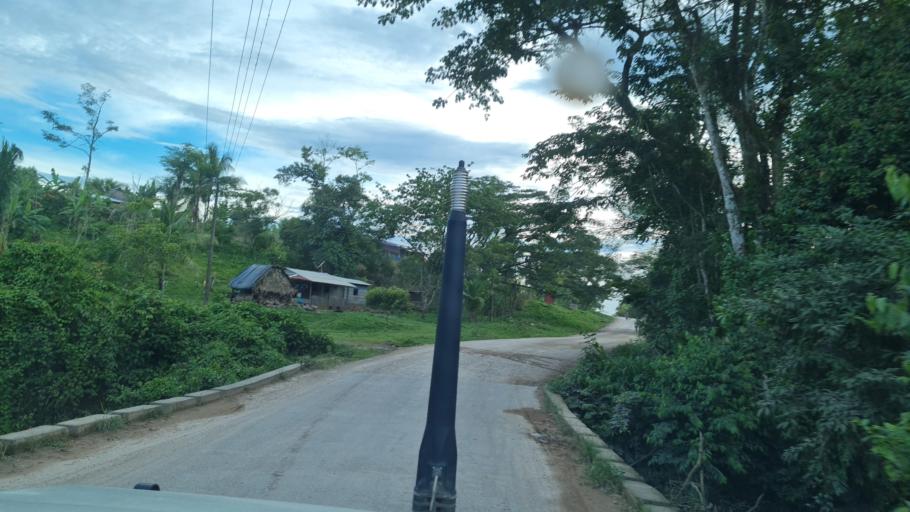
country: NI
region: Atlantico Norte (RAAN)
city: Siuna
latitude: 13.6870
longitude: -84.6121
